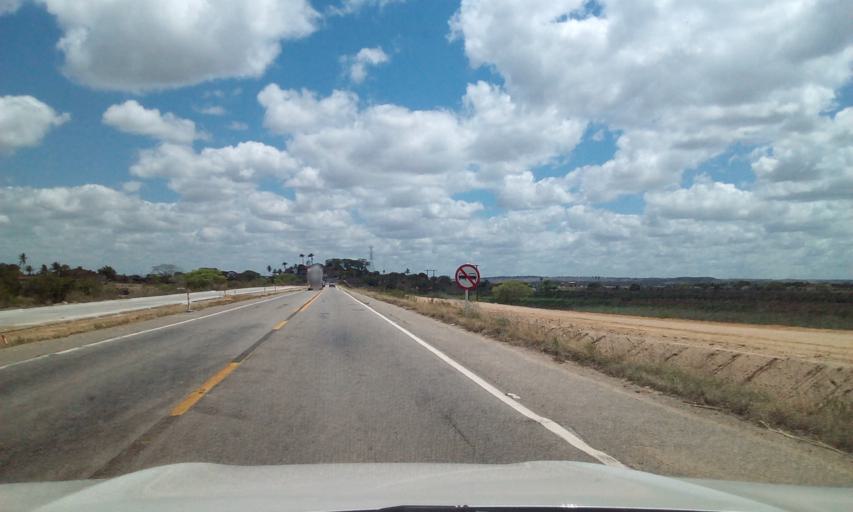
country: BR
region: Sergipe
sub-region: Propria
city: Propria
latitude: -10.2206
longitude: -36.8282
